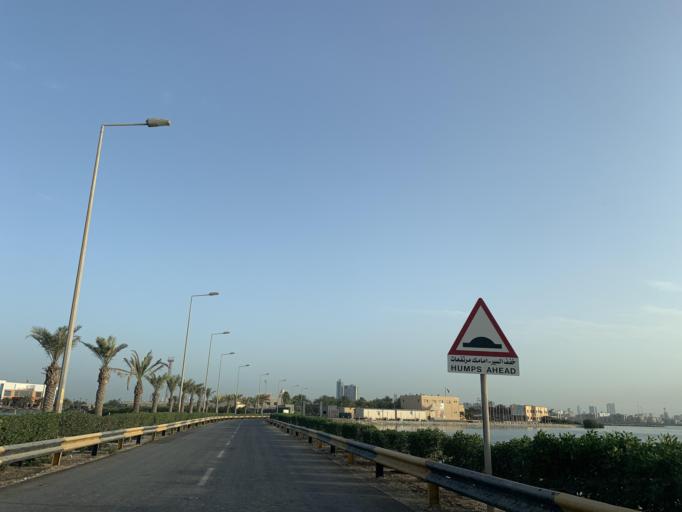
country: BH
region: Manama
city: Manama
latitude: 26.1873
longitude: 50.5860
